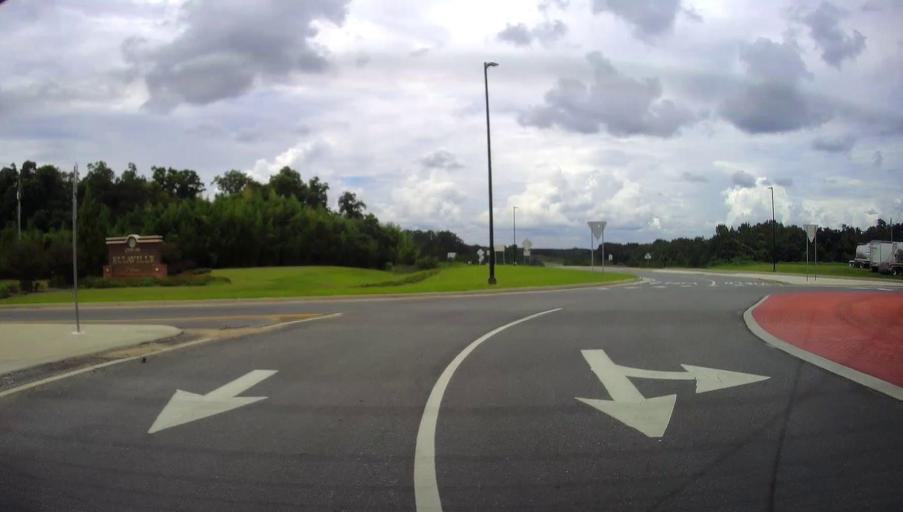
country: US
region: Georgia
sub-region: Schley County
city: Ellaville
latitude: 32.2397
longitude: -84.2966
